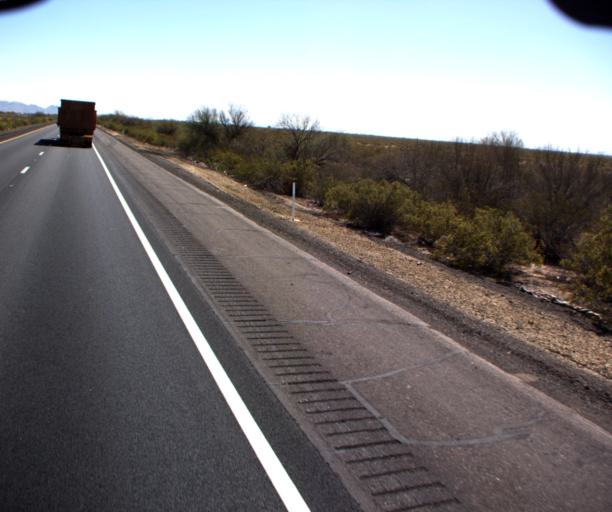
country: US
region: Arizona
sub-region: La Paz County
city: Salome
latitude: 33.6381
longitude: -113.8175
